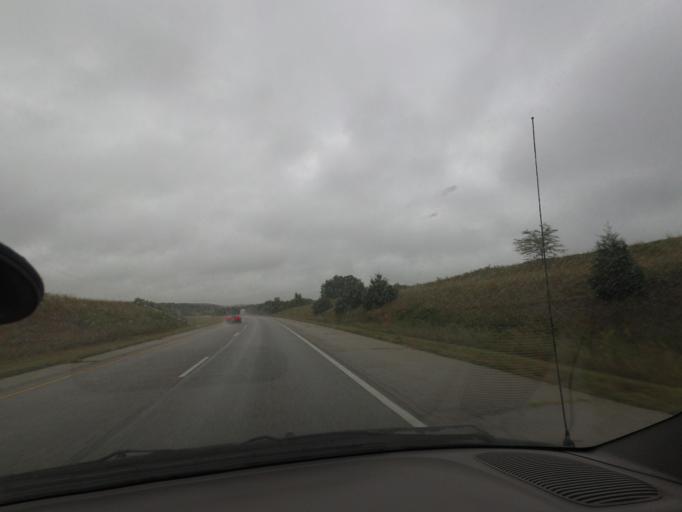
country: US
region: Illinois
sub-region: Pike County
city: Barry
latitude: 39.7274
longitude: -91.1212
